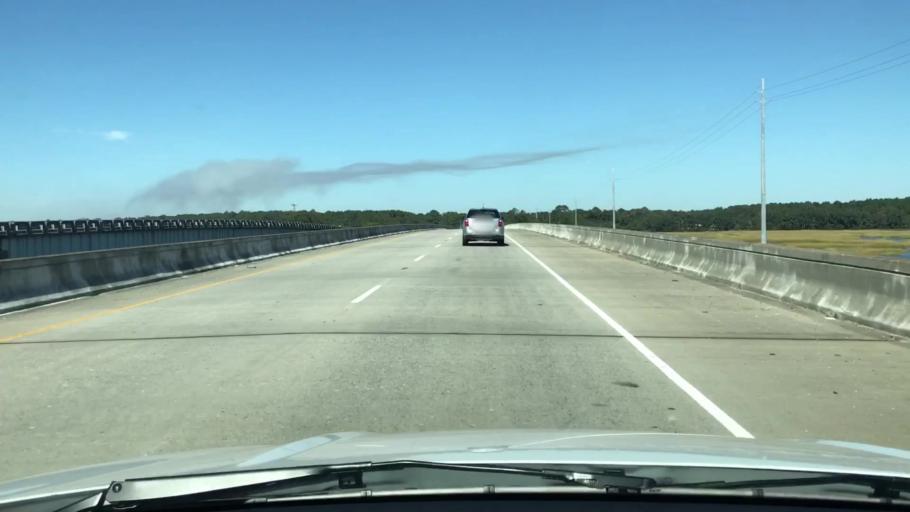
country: US
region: South Carolina
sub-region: Beaufort County
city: Laurel Bay
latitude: 32.5394
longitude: -80.7454
